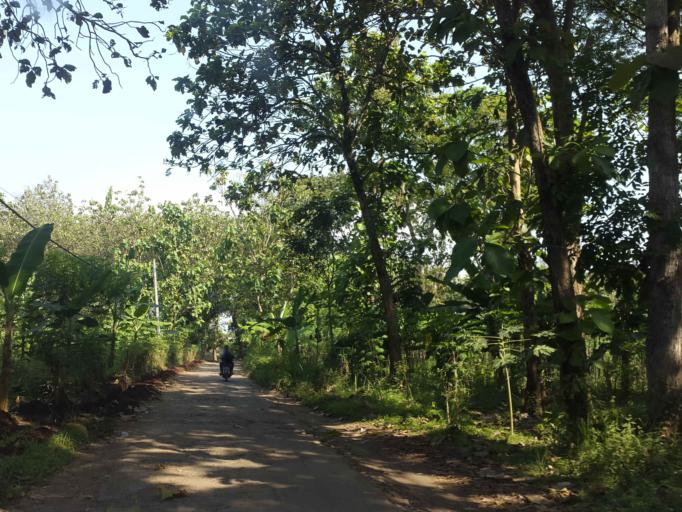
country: ID
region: West Java
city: Ciranjang-hilir
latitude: -6.7723
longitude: 107.2739
